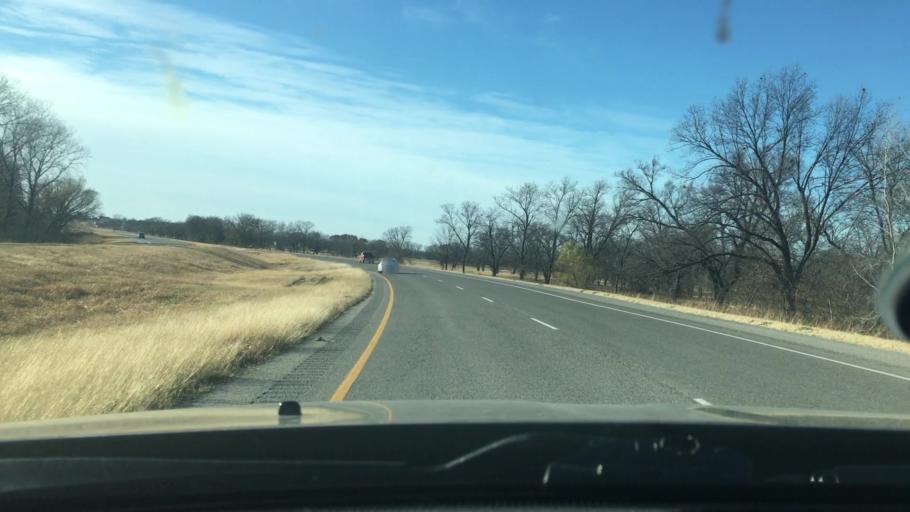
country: US
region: Oklahoma
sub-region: Murray County
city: Davis
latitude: 34.5061
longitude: -97.1480
